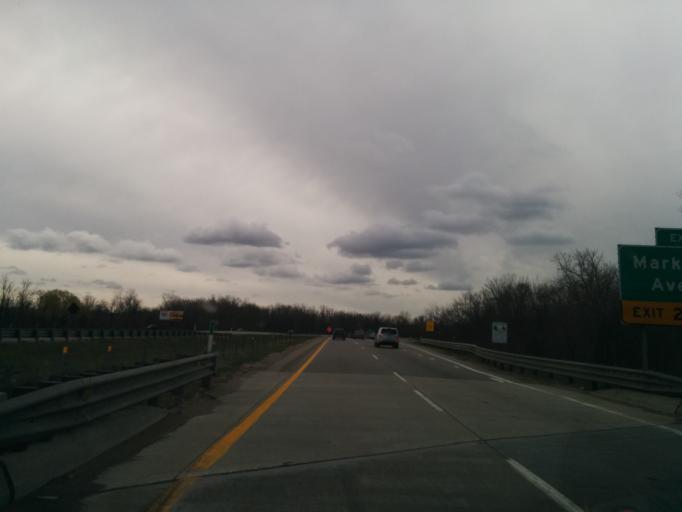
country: US
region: Michigan
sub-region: Kent County
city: Wyoming
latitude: 42.9465
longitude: -85.7113
